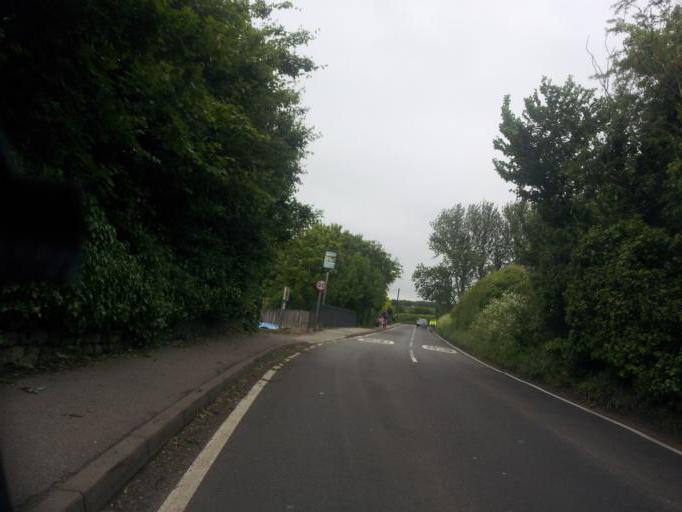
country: GB
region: England
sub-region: Kent
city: Maidstone
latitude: 51.2523
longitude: 0.4803
